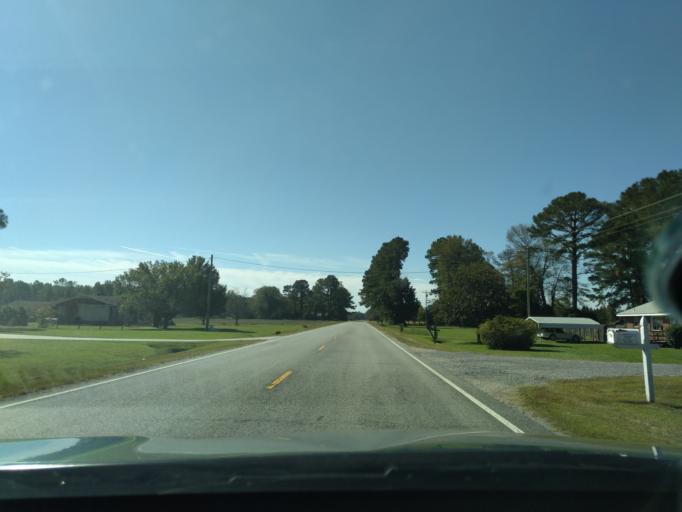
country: US
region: North Carolina
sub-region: Washington County
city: Plymouth
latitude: 35.6952
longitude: -76.7696
